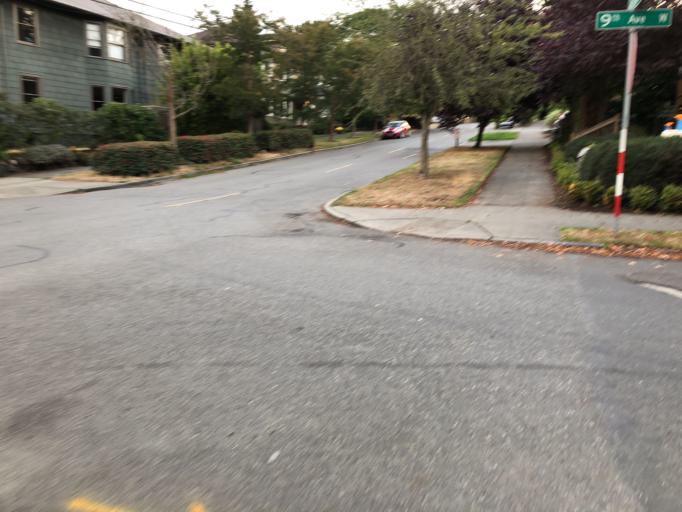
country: US
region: Washington
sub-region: King County
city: Seattle
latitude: 47.6395
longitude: -122.3690
